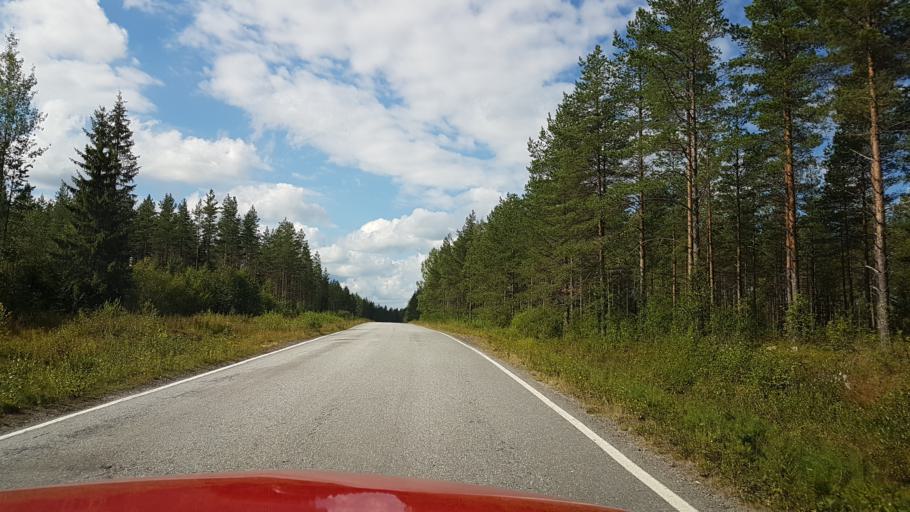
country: FI
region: Northern Ostrobothnia
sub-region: Ylivieska
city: Himanka
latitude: 64.0790
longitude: 23.7197
